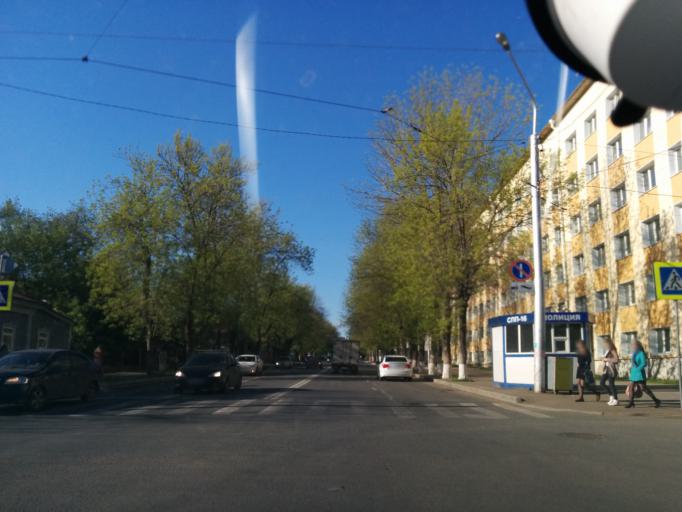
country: RU
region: Bashkortostan
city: Ufa
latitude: 54.7263
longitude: 55.9347
